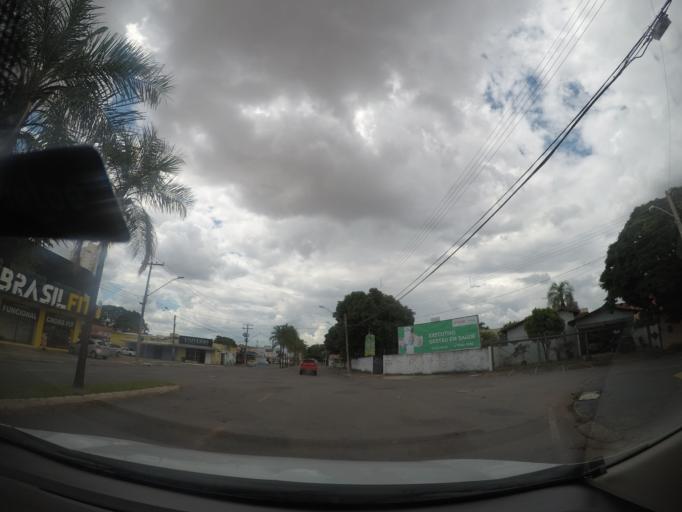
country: BR
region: Goias
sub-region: Goiania
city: Goiania
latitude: -16.7016
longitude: -49.2855
